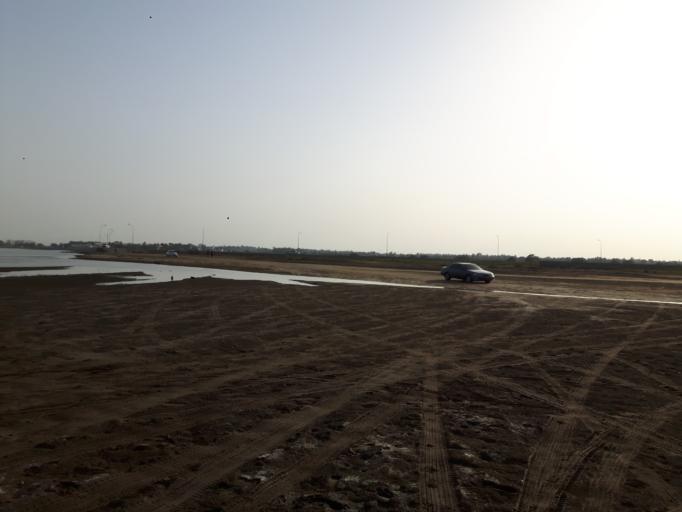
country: OM
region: Al Batinah
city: Al Sohar
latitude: 24.4096
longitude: 56.7159
